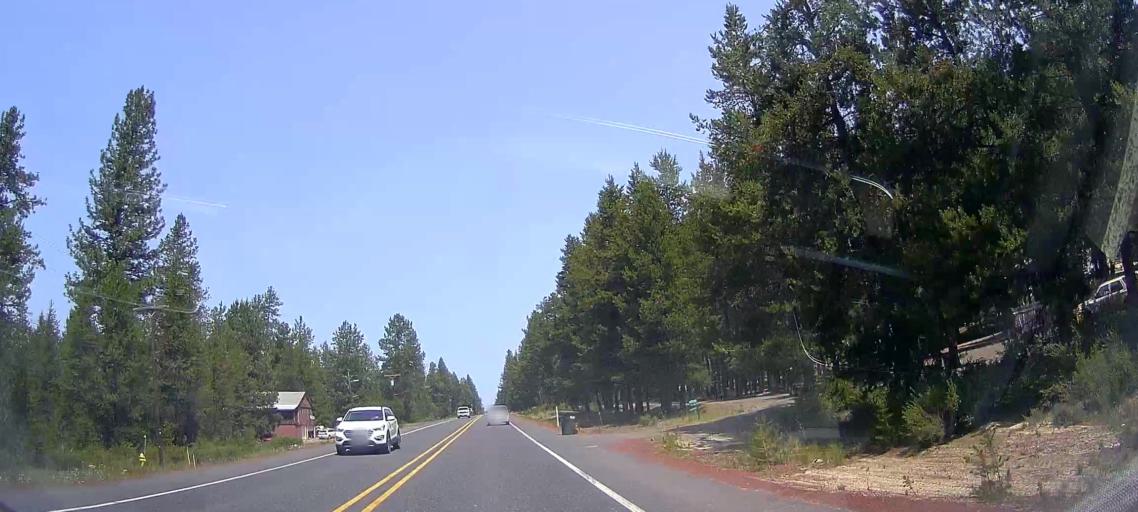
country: US
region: Oregon
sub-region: Deschutes County
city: La Pine
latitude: 43.4686
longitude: -121.6912
